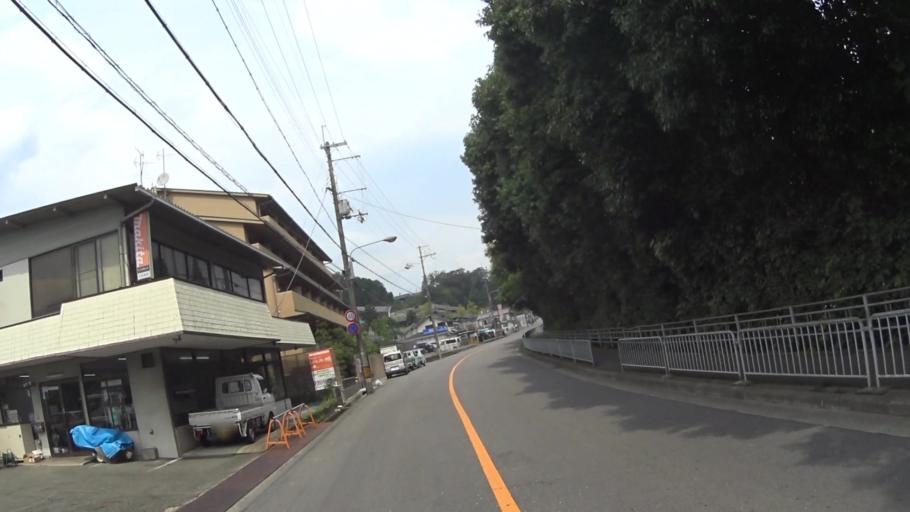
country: JP
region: Kyoto
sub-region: Kyoto-shi
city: Kamigyo-ku
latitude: 35.0703
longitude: 135.7538
